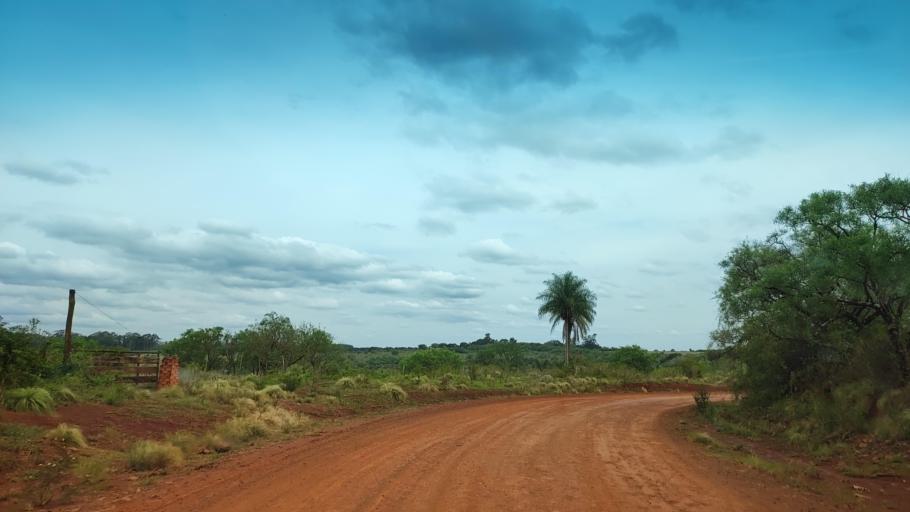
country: AR
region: Misiones
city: Garupa
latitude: -27.5147
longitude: -55.9708
